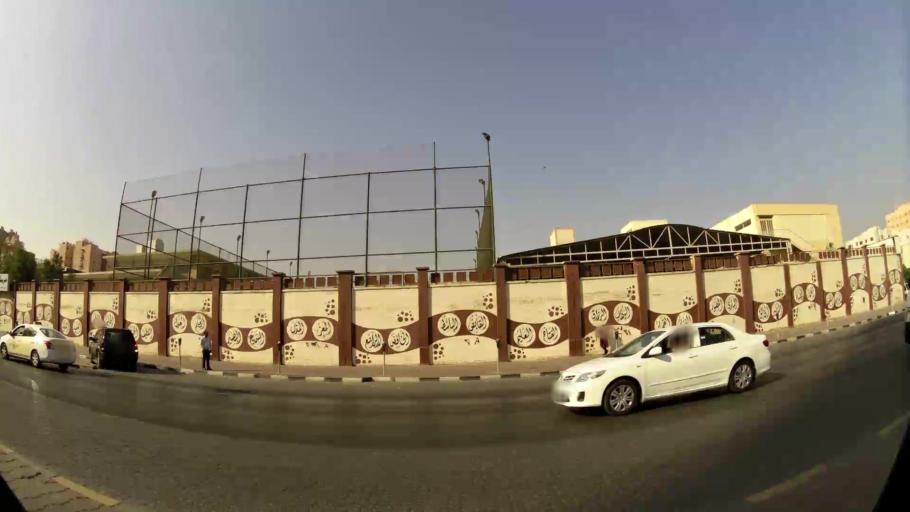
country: KW
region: Muhafazat Hawalli
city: Hawalli
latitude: 29.3314
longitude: 48.0274
